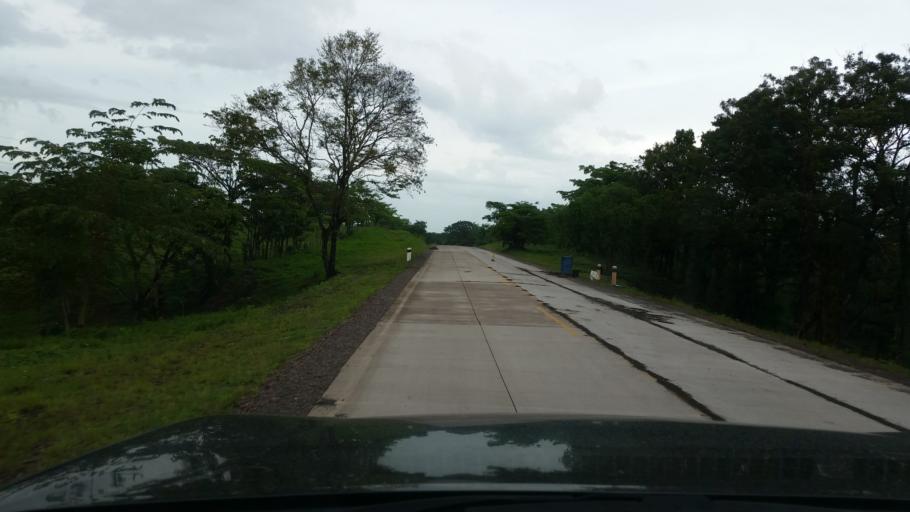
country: NI
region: Matagalpa
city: Rio Blanco
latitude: 13.1407
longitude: -85.0050
